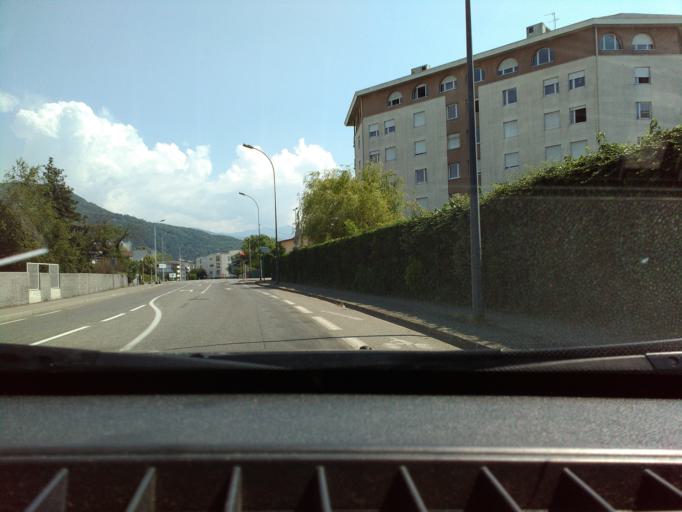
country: FR
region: Rhone-Alpes
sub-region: Departement de l'Isere
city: Saint-Martin-d'Heres
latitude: 45.1773
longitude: 5.7518
